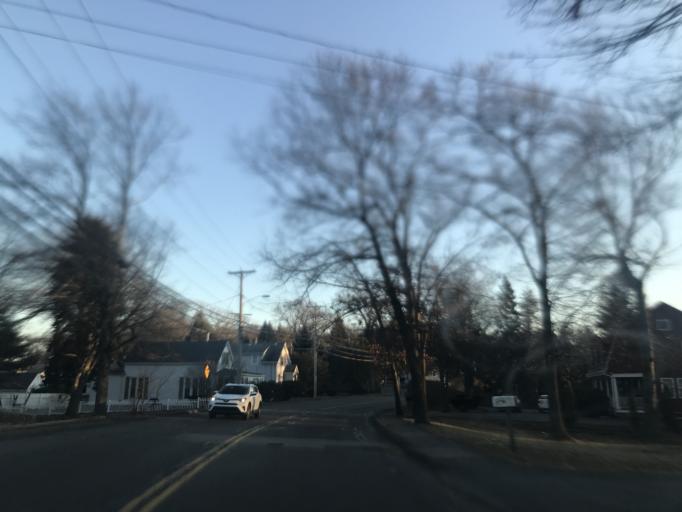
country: US
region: Massachusetts
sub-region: Essex County
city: Saugus
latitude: 42.4818
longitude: -71.0104
